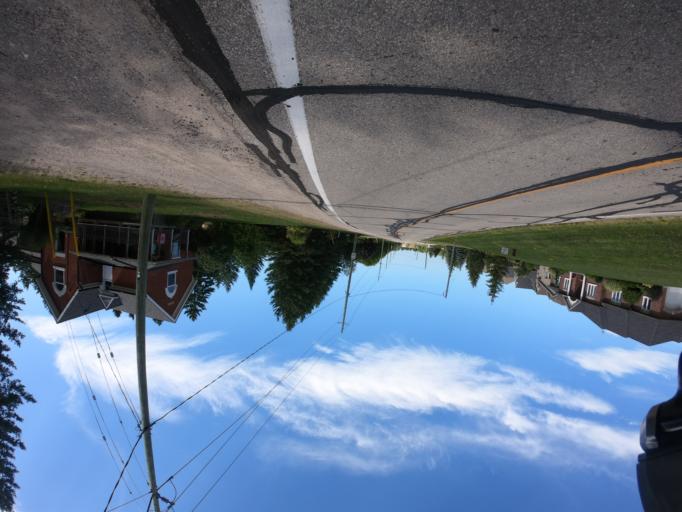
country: CA
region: Ontario
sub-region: Wellington County
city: Guelph
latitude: 43.5363
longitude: -80.3855
